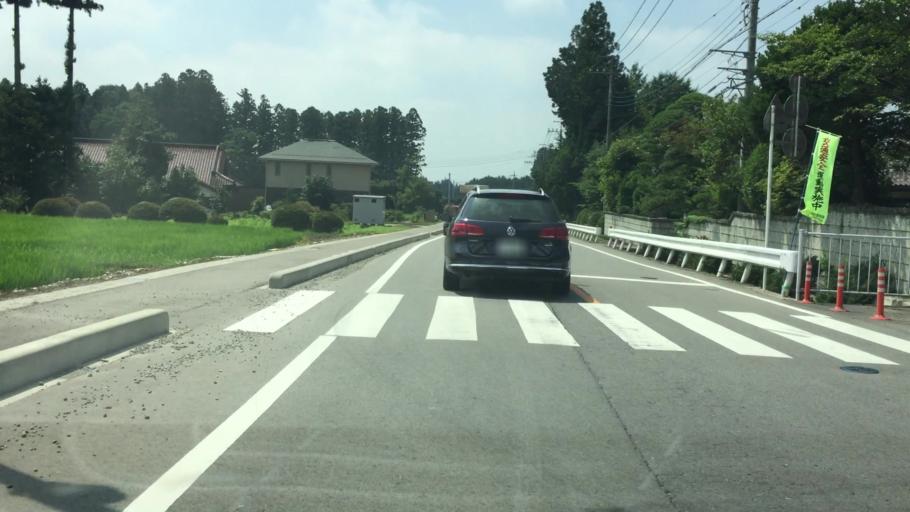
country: JP
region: Tochigi
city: Kuroiso
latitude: 36.9422
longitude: 139.9608
